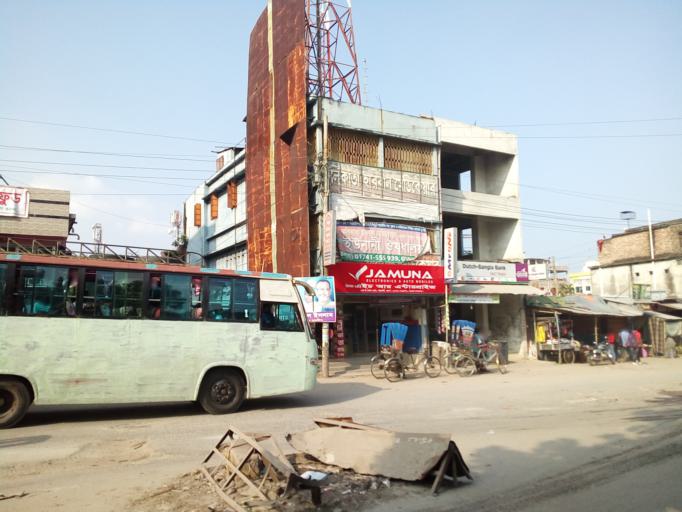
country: BD
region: Khulna
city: Khulna
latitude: 22.8010
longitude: 89.5409
